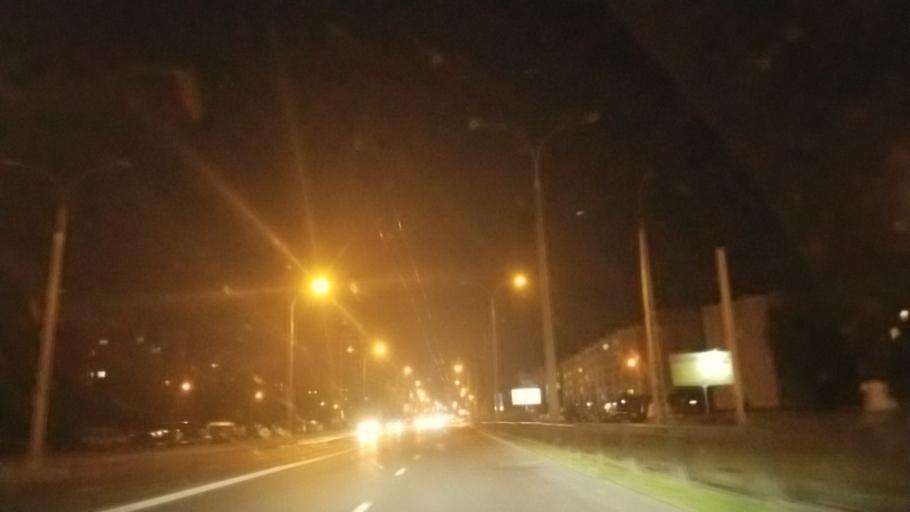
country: BY
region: Brest
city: Brest
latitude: 52.0706
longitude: 23.7512
